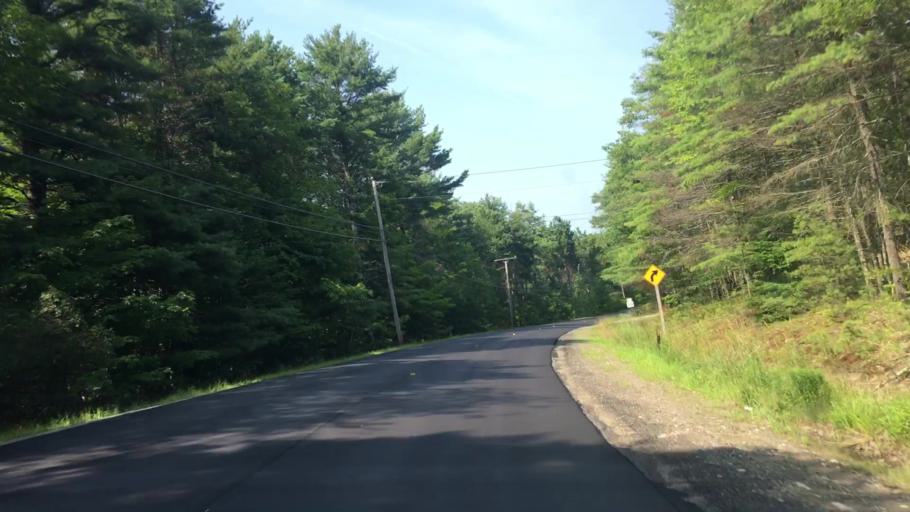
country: US
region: Maine
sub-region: Sagadahoc County
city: North Bath
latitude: 43.9405
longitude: -69.8001
